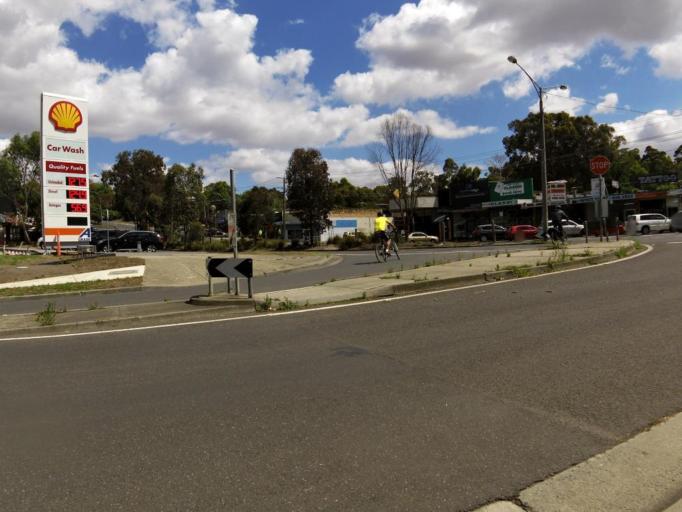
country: AU
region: Victoria
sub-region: Nillumbik
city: Diamond Creek
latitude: -37.6734
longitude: 145.1523
